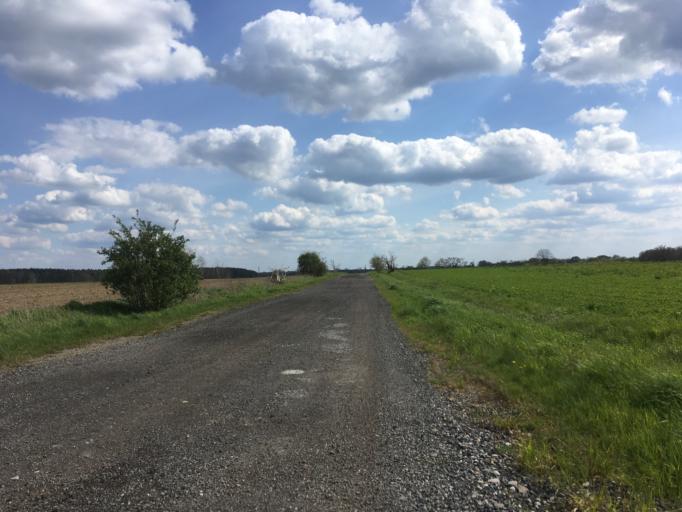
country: DE
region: Brandenburg
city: Werneuchen
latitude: 52.6033
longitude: 13.7013
